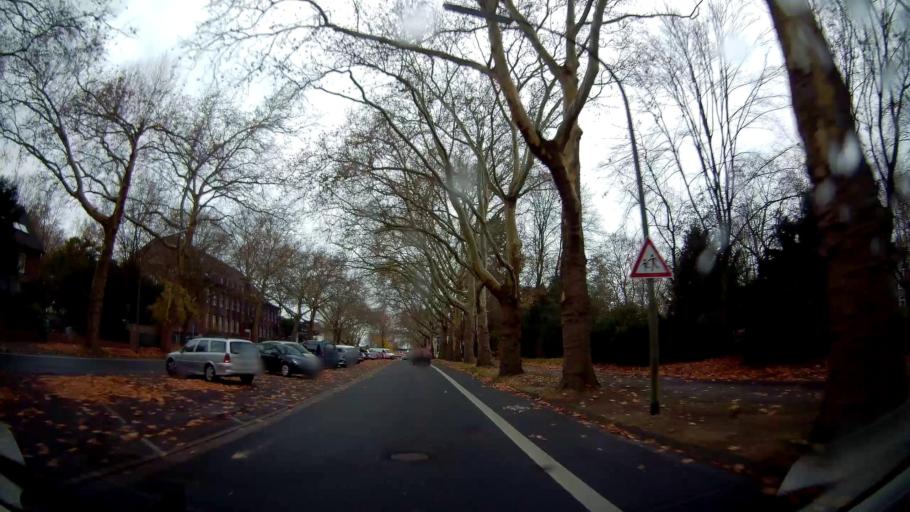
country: DE
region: North Rhine-Westphalia
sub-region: Regierungsbezirk Munster
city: Gelsenkirchen
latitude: 51.4944
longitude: 7.0823
